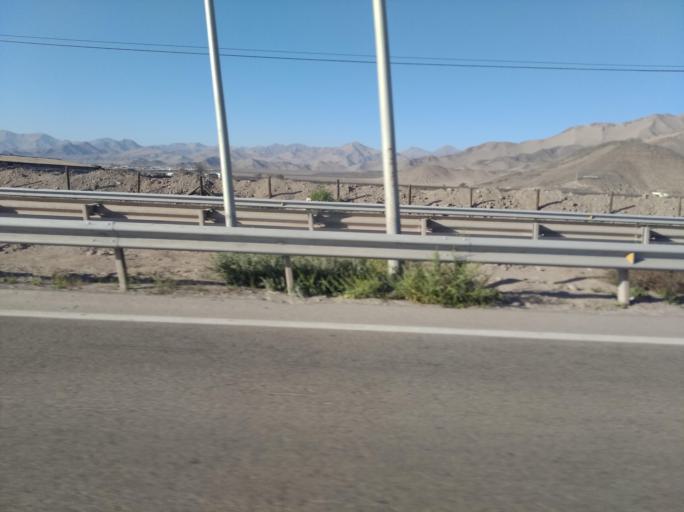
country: CL
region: Atacama
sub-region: Provincia de Copiapo
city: Copiapo
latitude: -27.3344
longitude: -70.3779
